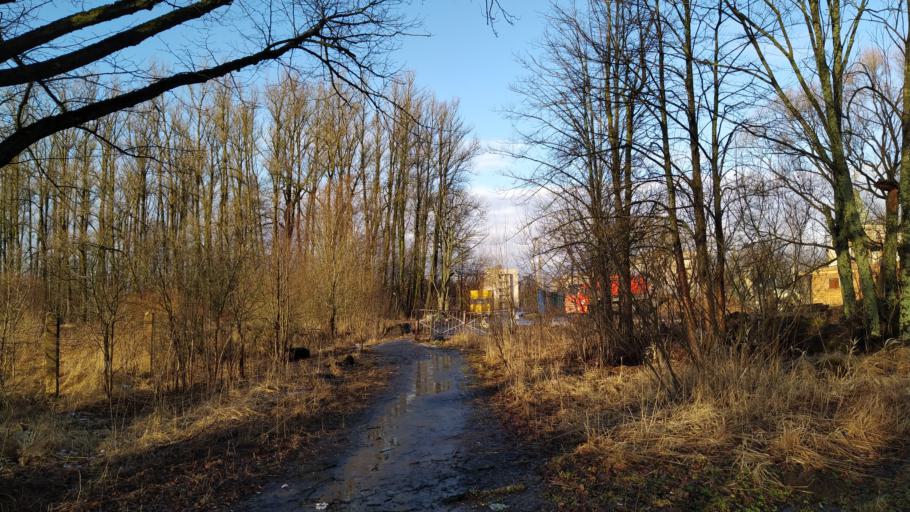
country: RU
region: St.-Petersburg
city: Pushkin
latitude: 59.7288
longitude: 30.3855
